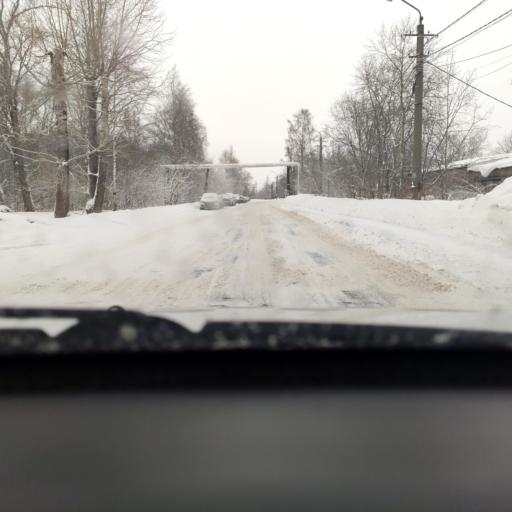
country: RU
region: Perm
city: Polazna
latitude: 58.1496
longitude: 56.4445
